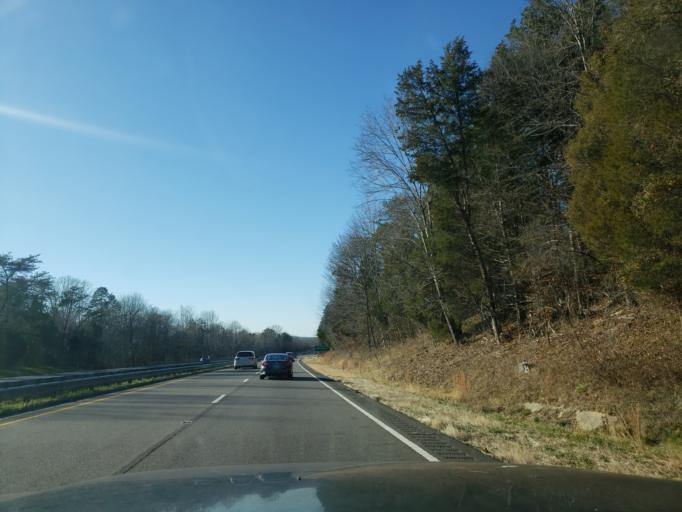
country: US
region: North Carolina
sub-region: Forsyth County
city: Lewisville
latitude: 36.1017
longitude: -80.4994
